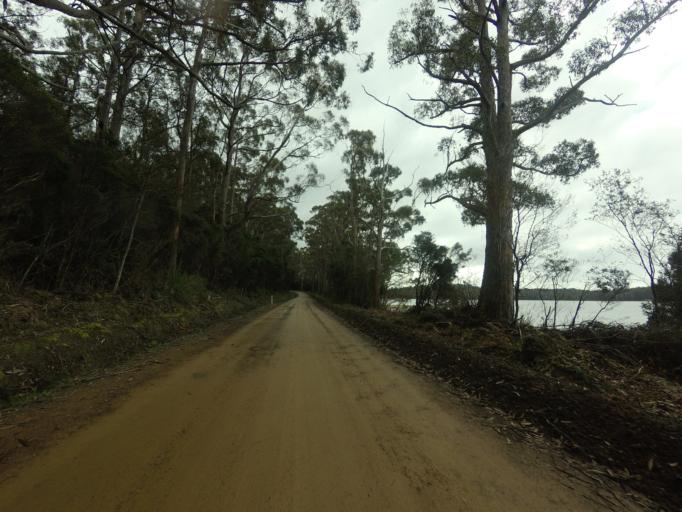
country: AU
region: Tasmania
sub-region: Huon Valley
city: Geeveston
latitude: -43.5317
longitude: 146.8939
